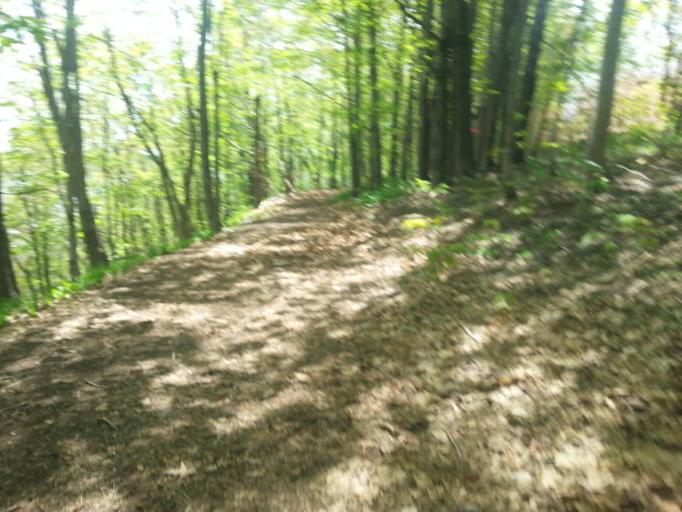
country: CA
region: Quebec
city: Quebec
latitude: 46.7710
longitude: -71.2554
